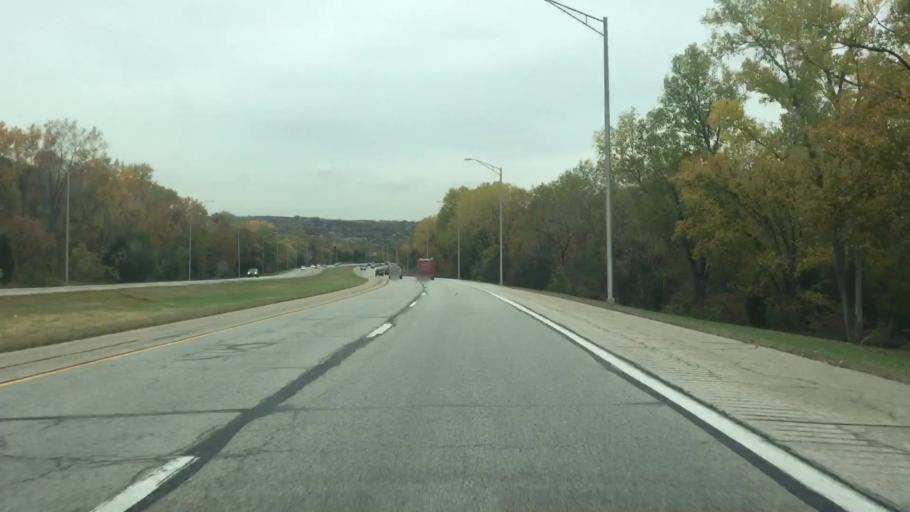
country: US
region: Kansas
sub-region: Wyandotte County
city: Edwardsville
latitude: 39.0106
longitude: -94.8002
